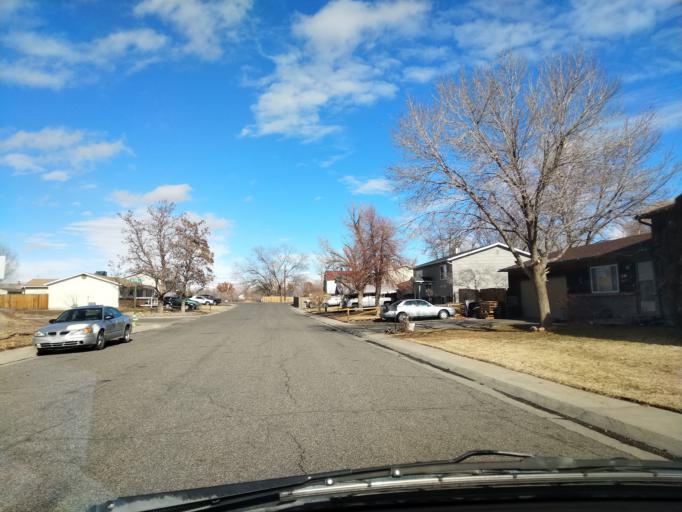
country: US
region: Colorado
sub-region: Mesa County
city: Fruitvale
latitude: 39.0761
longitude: -108.4878
